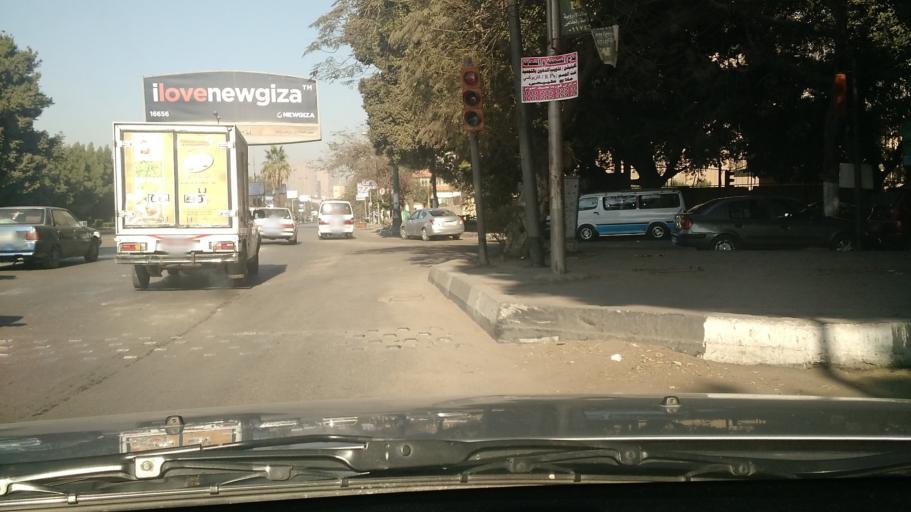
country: EG
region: Al Jizah
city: Al Hawamidiyah
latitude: 29.9595
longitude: 31.2486
